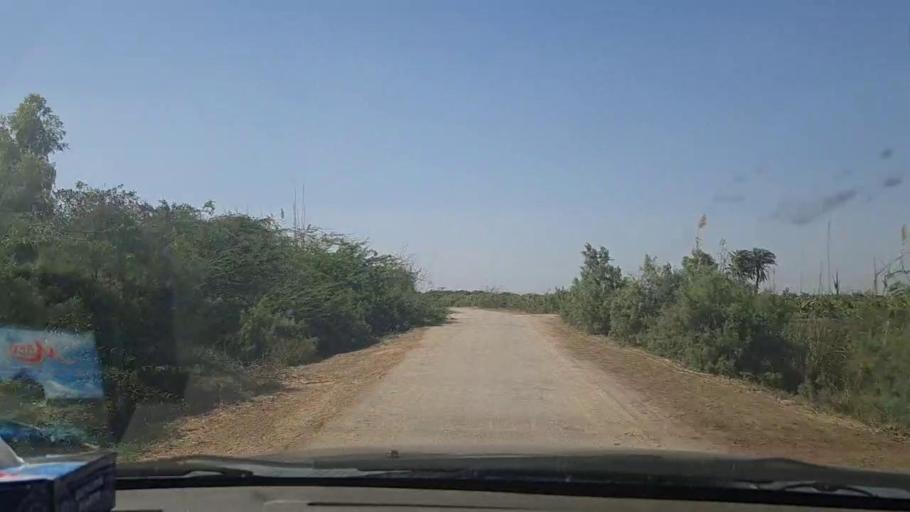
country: PK
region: Sindh
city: Chuhar Jamali
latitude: 24.2864
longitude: 67.7588
